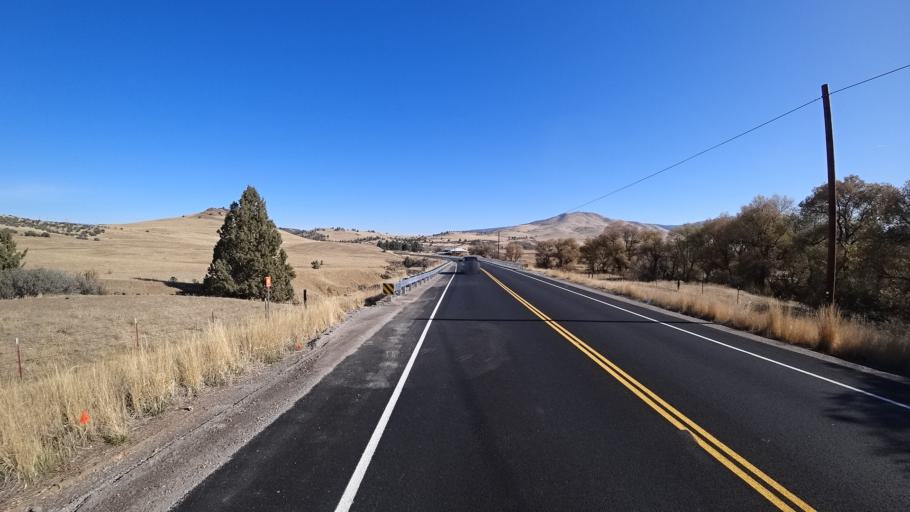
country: US
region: California
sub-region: Siskiyou County
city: Montague
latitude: 41.8462
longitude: -122.4724
